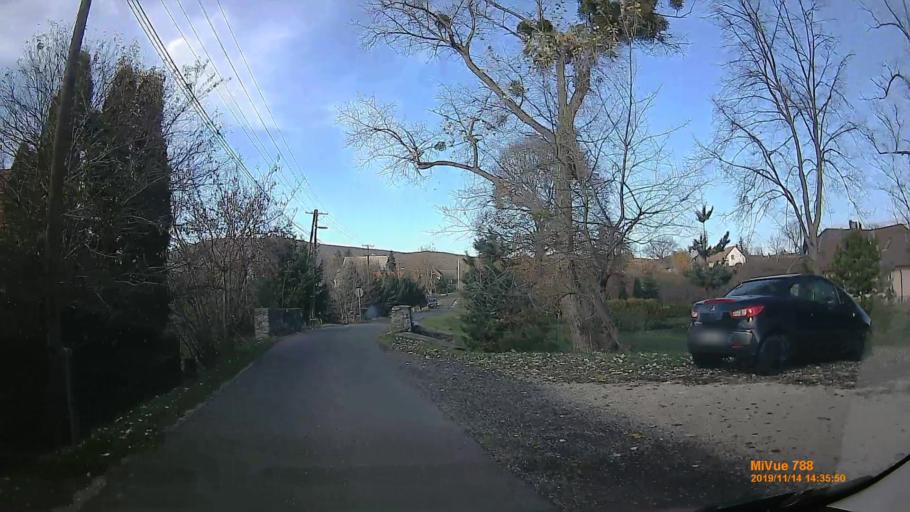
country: HU
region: Veszprem
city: Zirc
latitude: 47.2278
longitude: 17.7902
